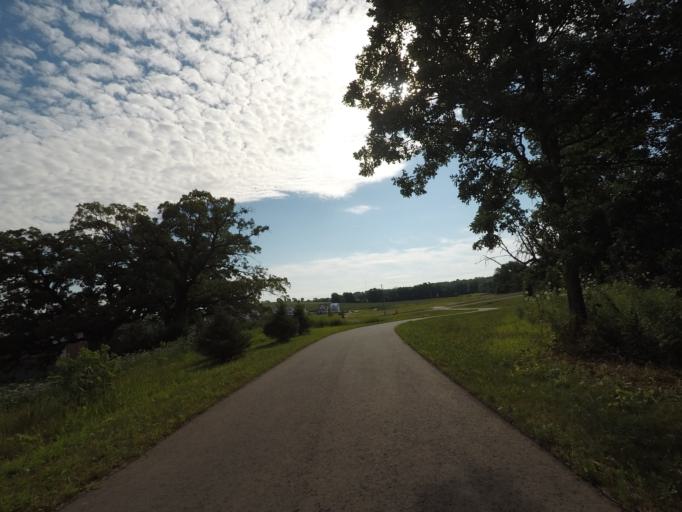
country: US
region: Wisconsin
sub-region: Dane County
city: Verona
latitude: 43.0487
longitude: -89.5538
